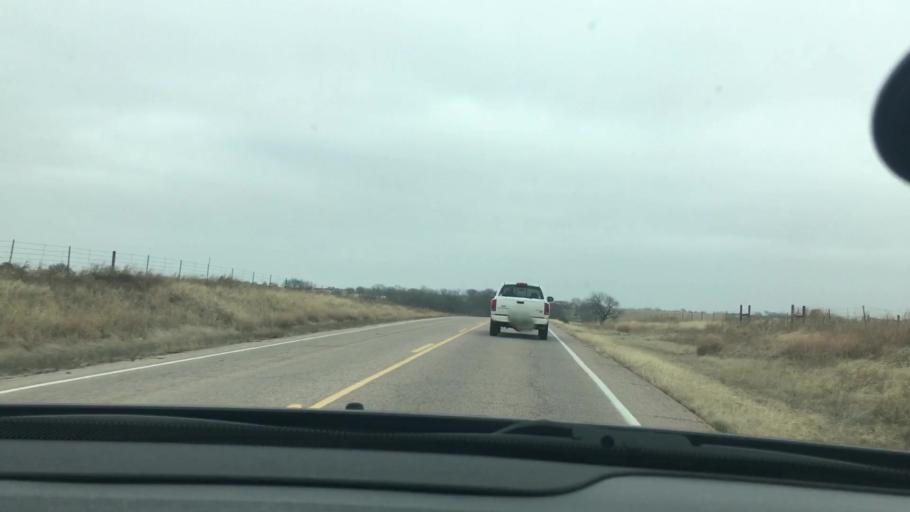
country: US
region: Oklahoma
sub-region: Marshall County
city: Madill
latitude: 34.1224
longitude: -96.7294
